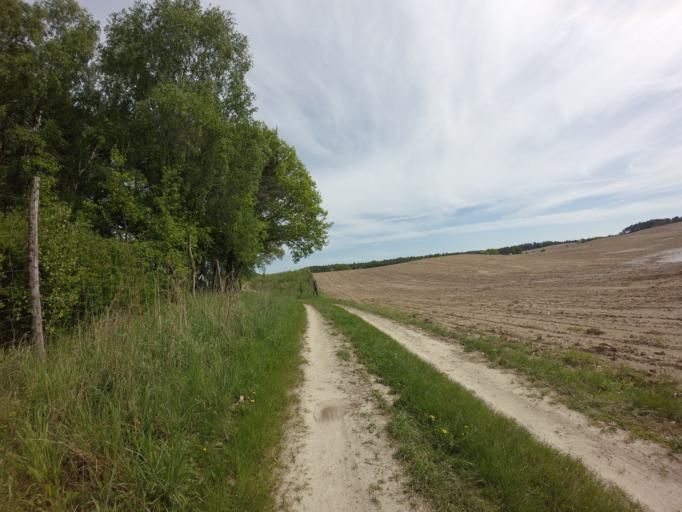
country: PL
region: West Pomeranian Voivodeship
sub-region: Powiat choszczenski
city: Recz
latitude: 53.1578
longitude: 15.5766
